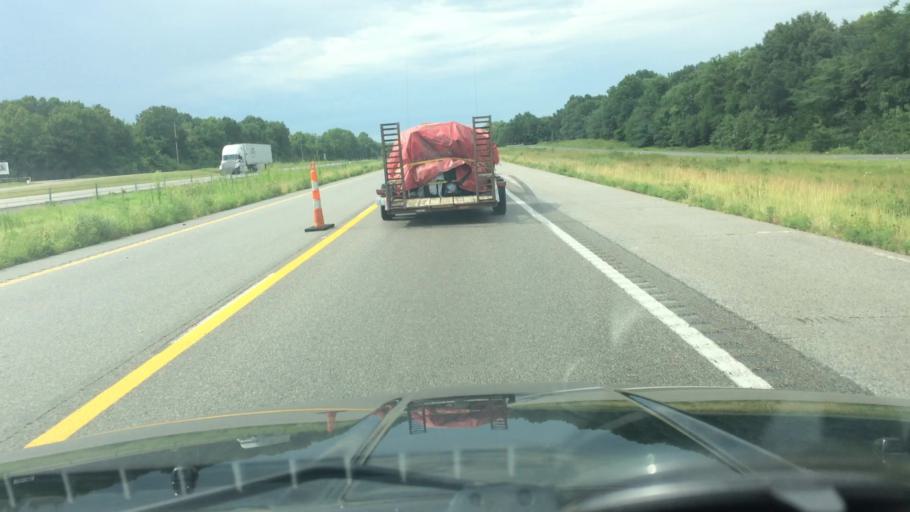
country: US
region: Missouri
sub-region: Cass County
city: Peculiar
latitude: 38.6840
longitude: -94.4230
